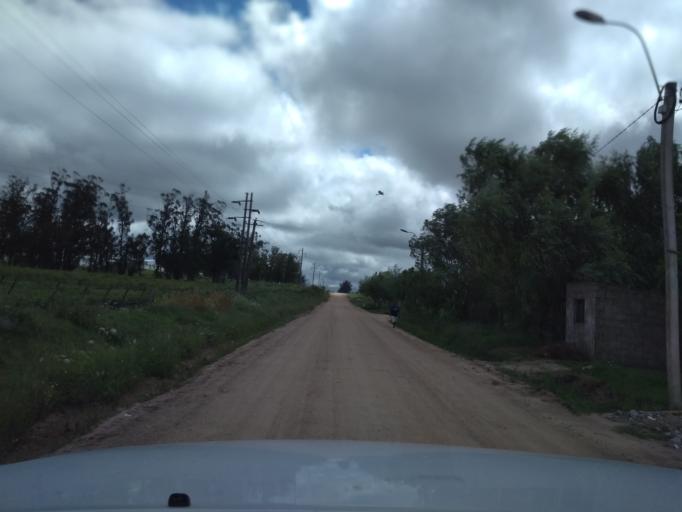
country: UY
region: Canelones
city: Pando
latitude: -34.6958
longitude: -55.9713
